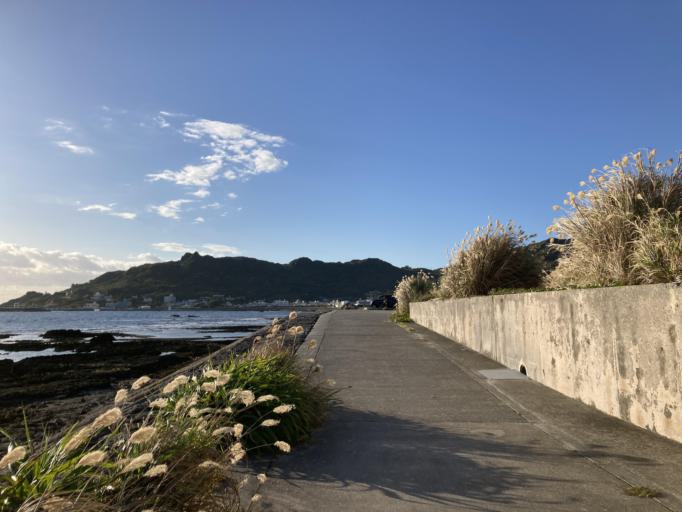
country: JP
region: Okinawa
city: Ginowan
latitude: 26.1874
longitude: 127.8225
